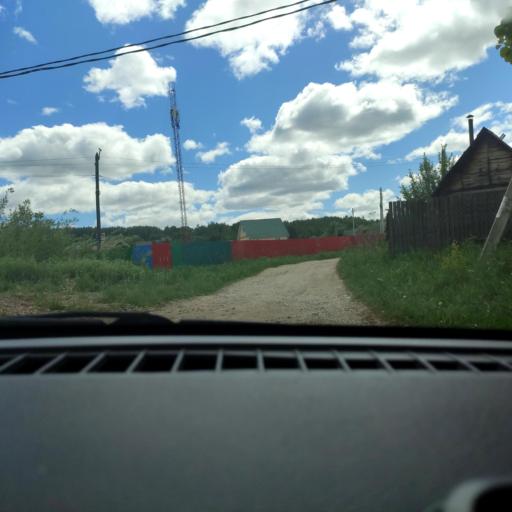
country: RU
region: Perm
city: Kondratovo
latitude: 58.0870
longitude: 56.0136
